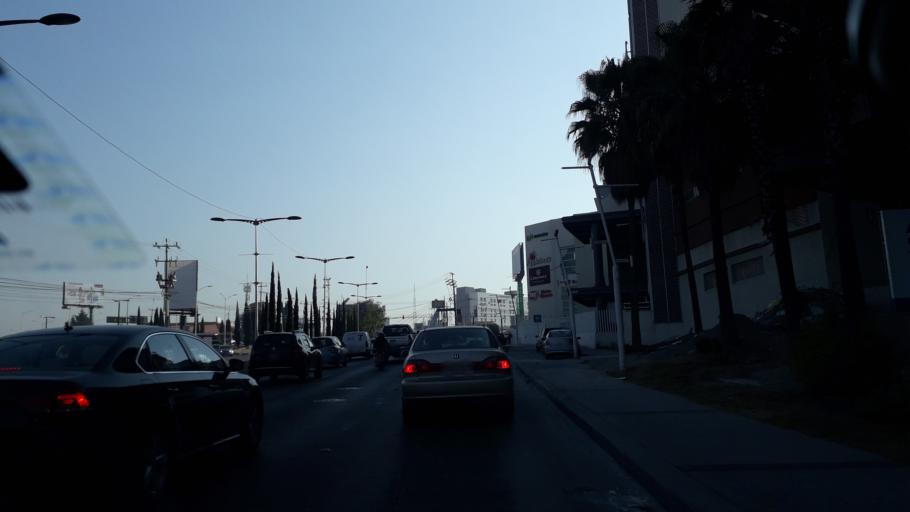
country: MX
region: Puebla
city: Puebla
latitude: 19.0433
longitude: -98.2364
